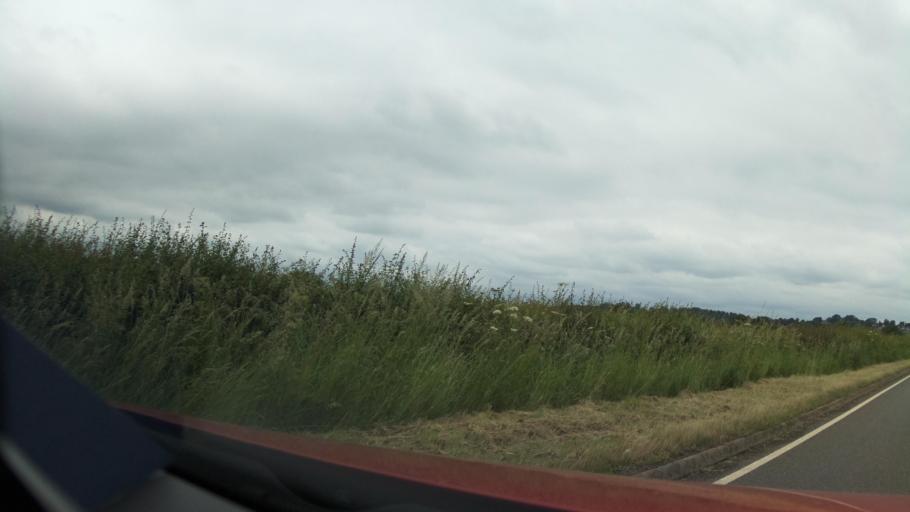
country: GB
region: England
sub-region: Leicestershire
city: Melton Mowbray
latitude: 52.7327
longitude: -0.8487
